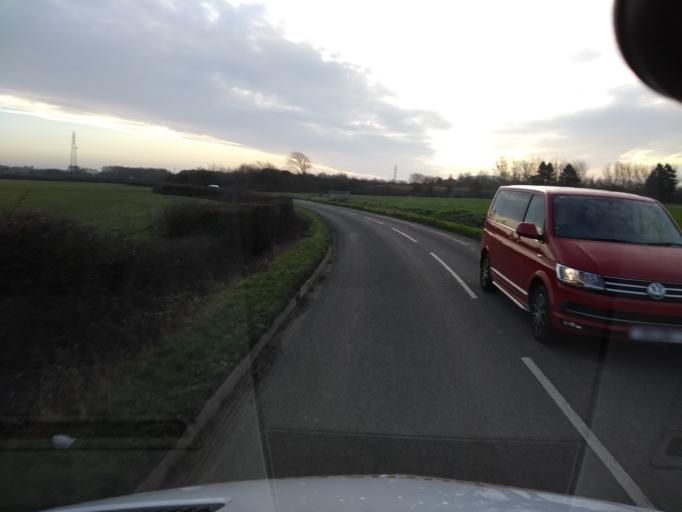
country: GB
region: England
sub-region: North Somerset
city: Bleadon
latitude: 51.2859
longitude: -2.9803
